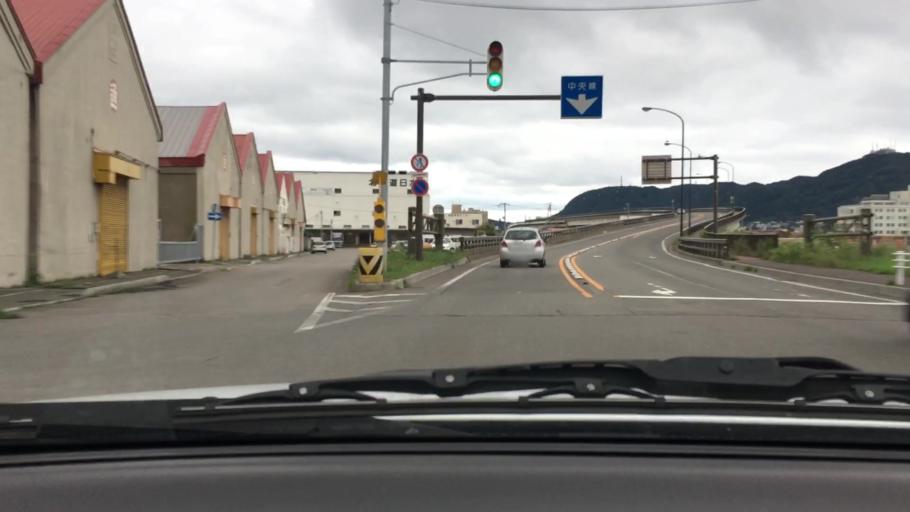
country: JP
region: Hokkaido
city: Hakodate
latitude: 41.7864
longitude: 140.7281
